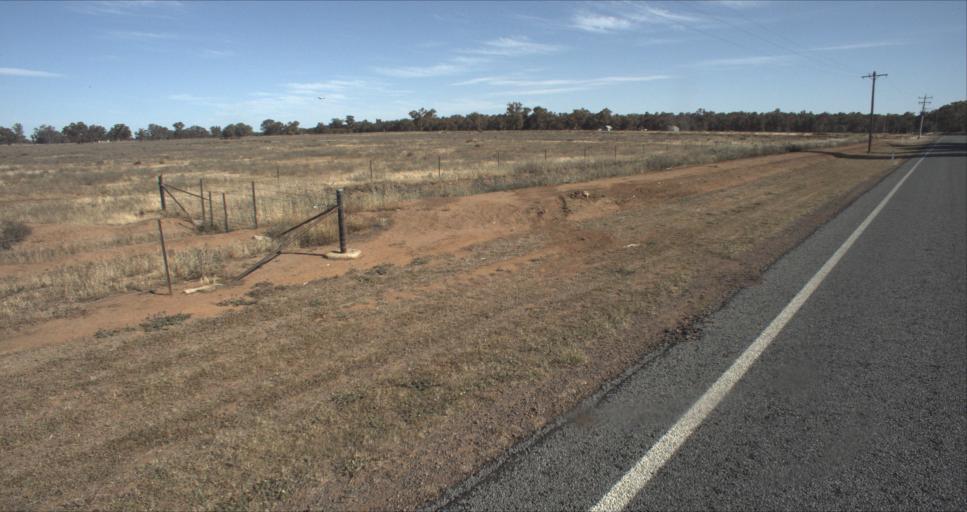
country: AU
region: New South Wales
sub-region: Leeton
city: Leeton
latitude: -34.6201
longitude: 146.3978
